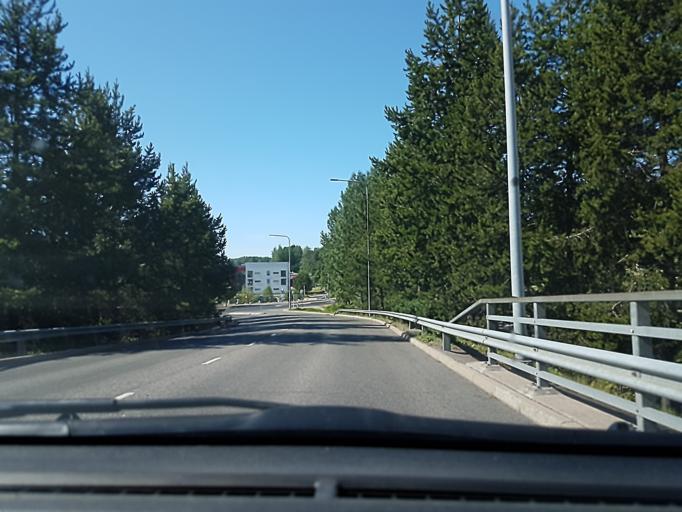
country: FI
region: Uusimaa
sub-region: Helsinki
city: Vantaa
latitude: 60.3307
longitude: 25.0614
